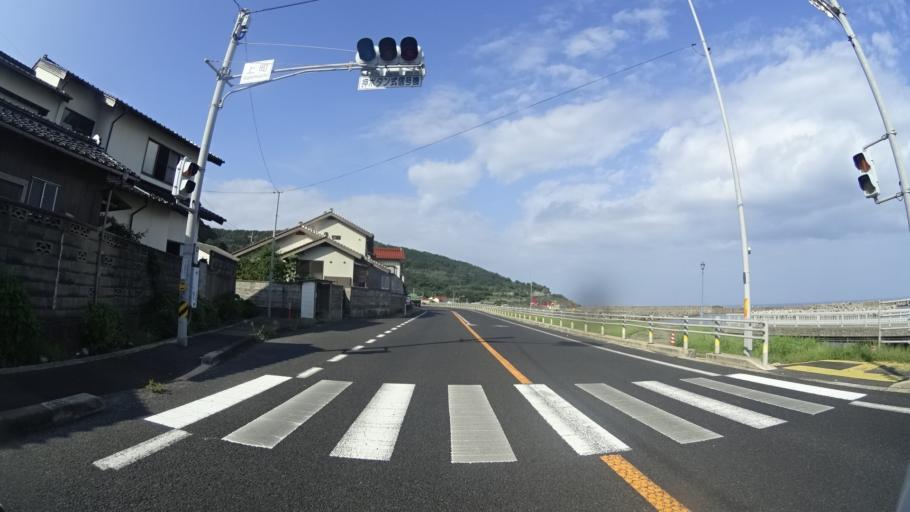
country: JP
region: Shimane
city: Odacho-oda
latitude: 35.2725
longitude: 132.5845
